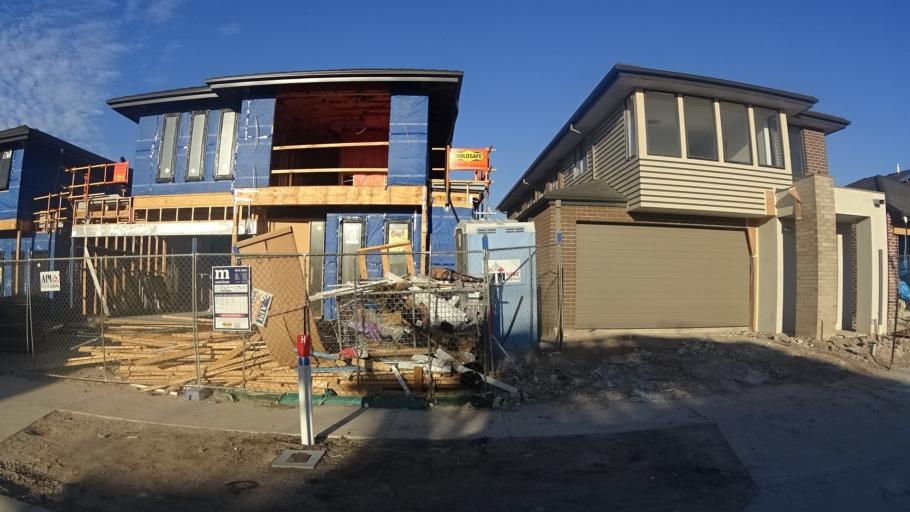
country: AU
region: Victoria
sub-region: Knox
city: Knoxfield
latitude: -37.8833
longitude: 145.2371
